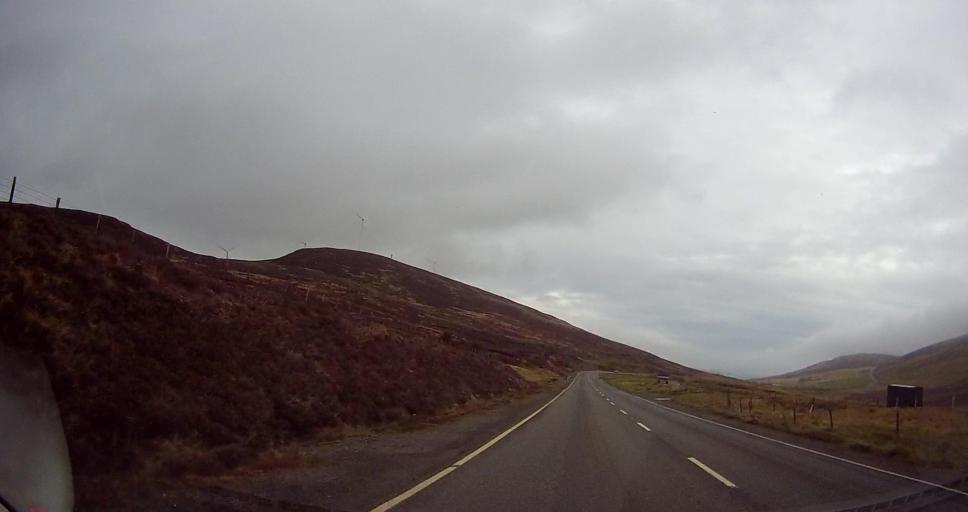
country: GB
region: Scotland
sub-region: Shetland Islands
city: Lerwick
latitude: 60.1545
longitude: -1.2352
